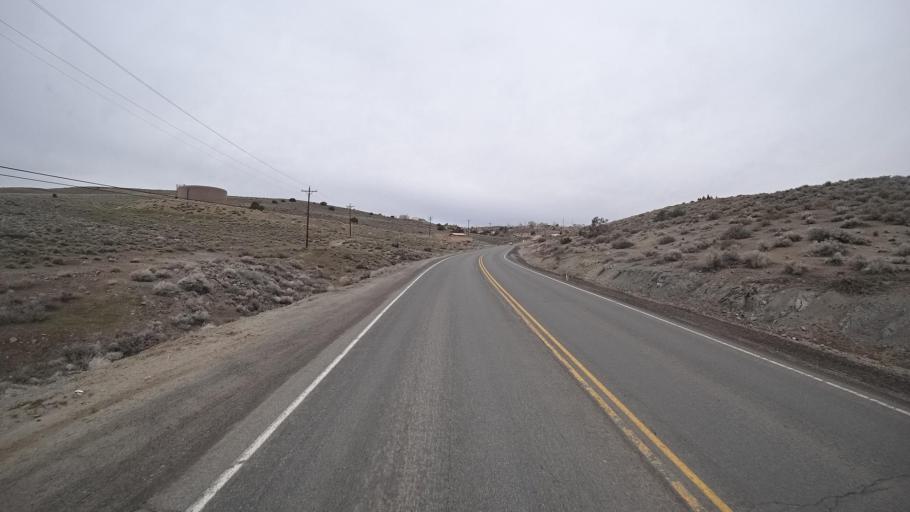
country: US
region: Nevada
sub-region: Washoe County
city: Sun Valley
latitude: 39.5990
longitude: -119.7922
